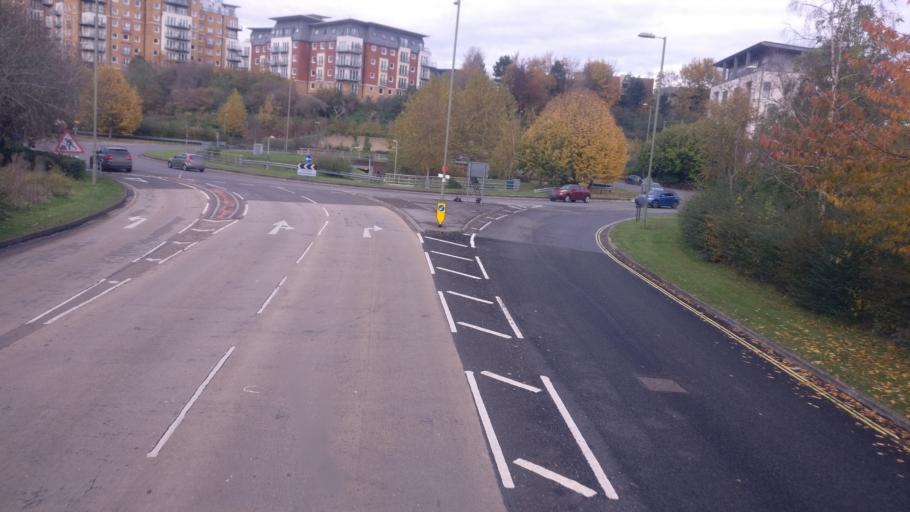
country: GB
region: England
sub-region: Hampshire
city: Basingstoke
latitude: 51.2658
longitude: -1.0923
